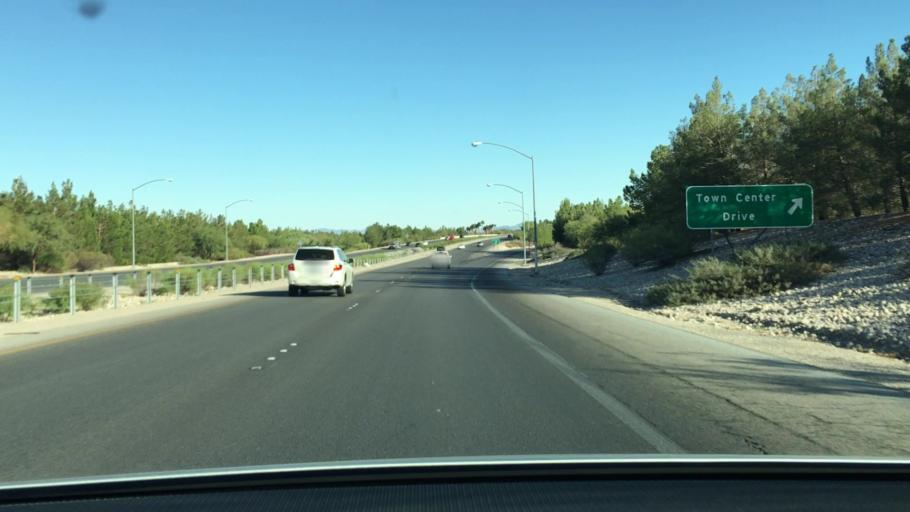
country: US
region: Nevada
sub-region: Clark County
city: Summerlin South
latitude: 36.1904
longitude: -115.3123
